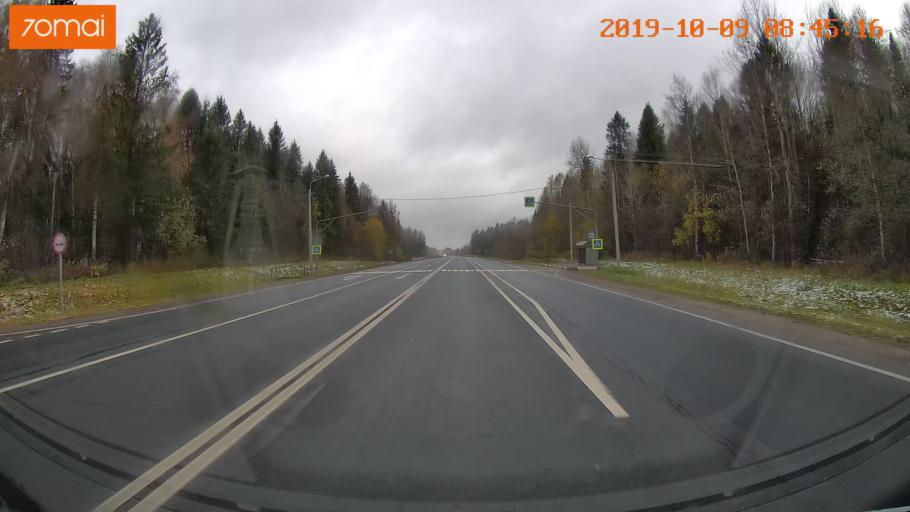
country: RU
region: Vologda
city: Gryazovets
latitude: 59.0464
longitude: 40.0939
